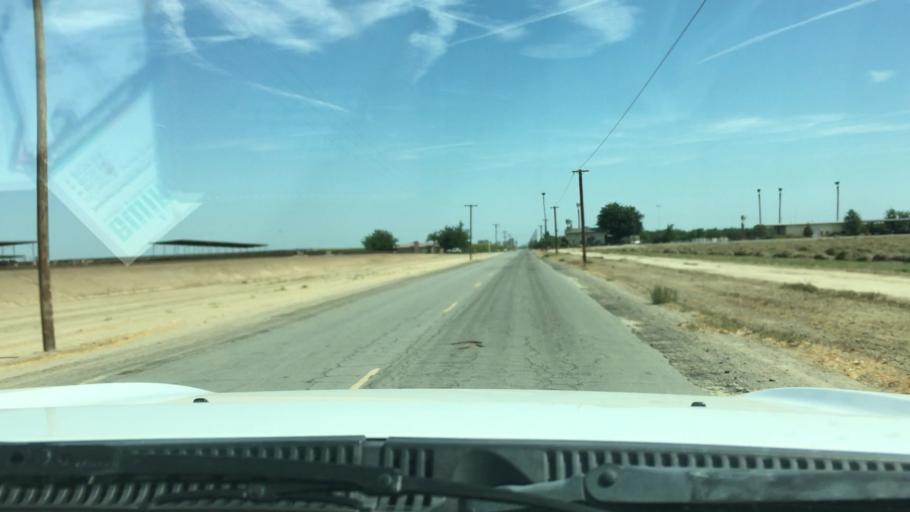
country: US
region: California
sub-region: Kern County
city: Buttonwillow
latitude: 35.4175
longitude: -119.3764
